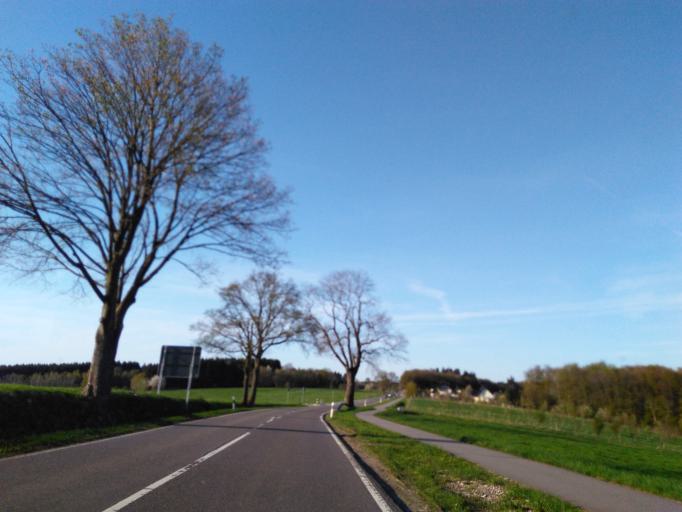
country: DE
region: North Rhine-Westphalia
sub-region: Regierungsbezirk Koln
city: Much
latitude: 50.9481
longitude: 7.4537
